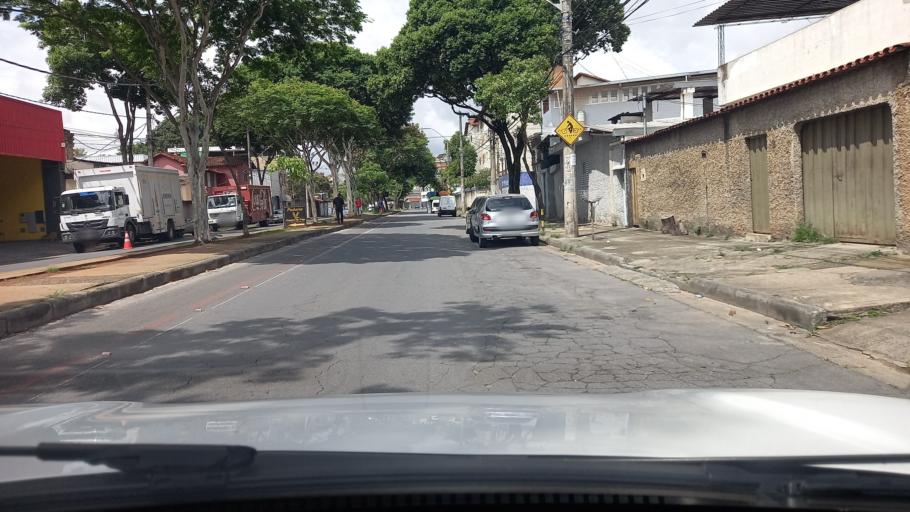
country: BR
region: Minas Gerais
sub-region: Contagem
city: Contagem
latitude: -19.8962
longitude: -44.0142
